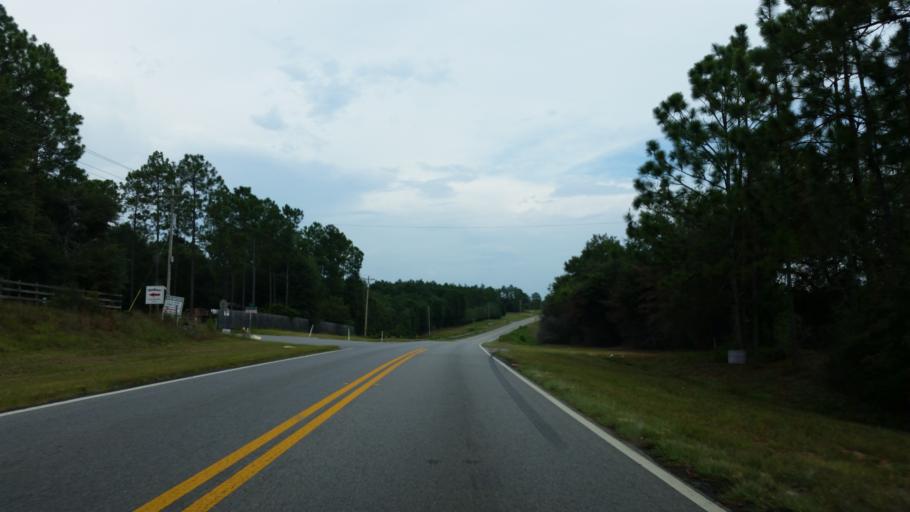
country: US
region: Florida
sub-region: Santa Rosa County
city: Wallace
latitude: 30.6726
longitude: -87.2239
